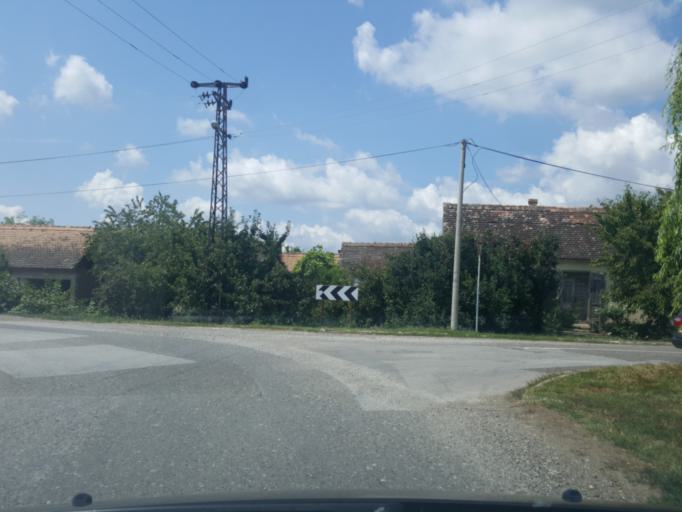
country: RS
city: Glusci
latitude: 44.9270
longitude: 19.5454
